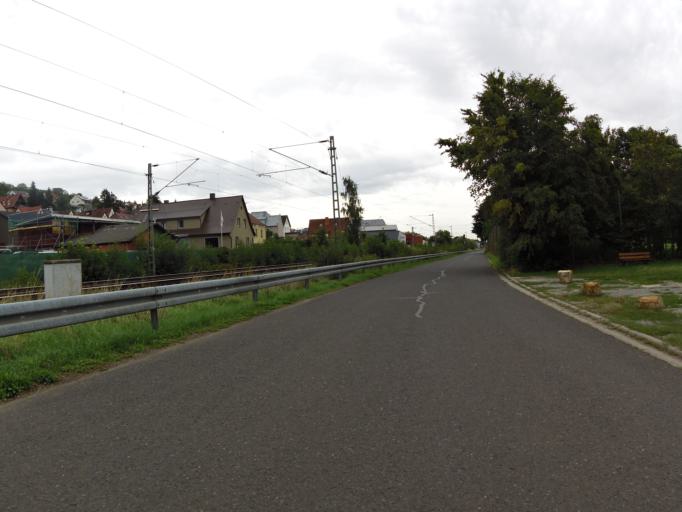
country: DE
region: Bavaria
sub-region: Regierungsbezirk Unterfranken
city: Schonungen
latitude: 50.0475
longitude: 10.3068
